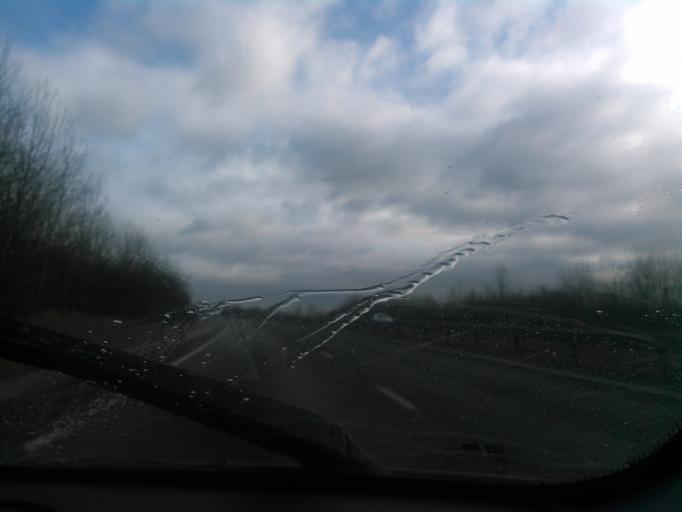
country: GB
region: England
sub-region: Derbyshire
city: Rodsley
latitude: 52.8825
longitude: -1.7204
